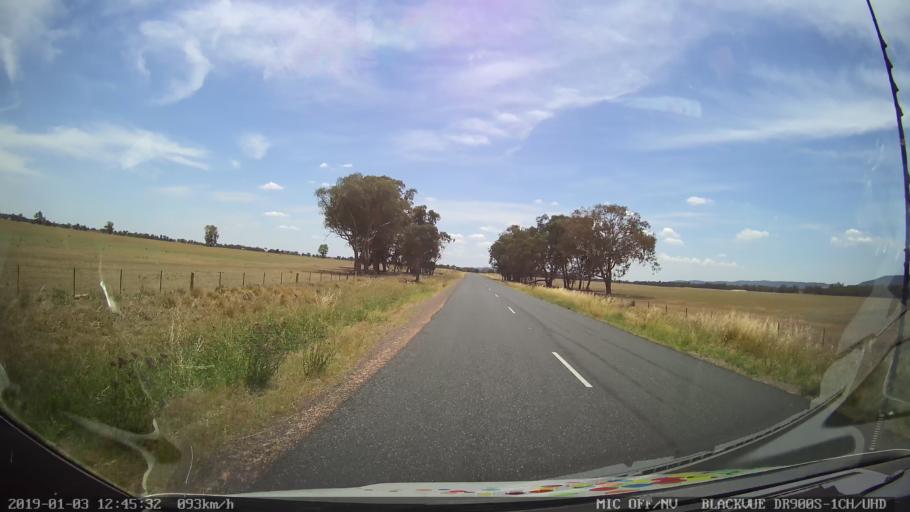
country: AU
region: New South Wales
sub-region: Weddin
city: Grenfell
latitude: -33.7484
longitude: 148.2244
